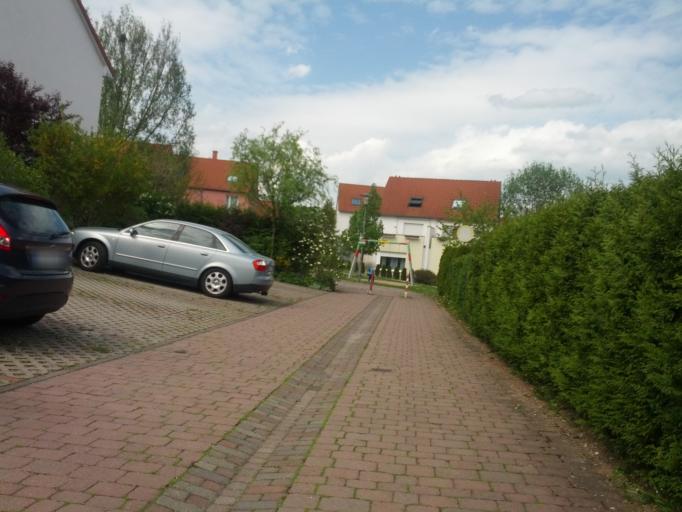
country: DE
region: Thuringia
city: Eisenach
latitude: 50.9911
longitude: 10.2919
